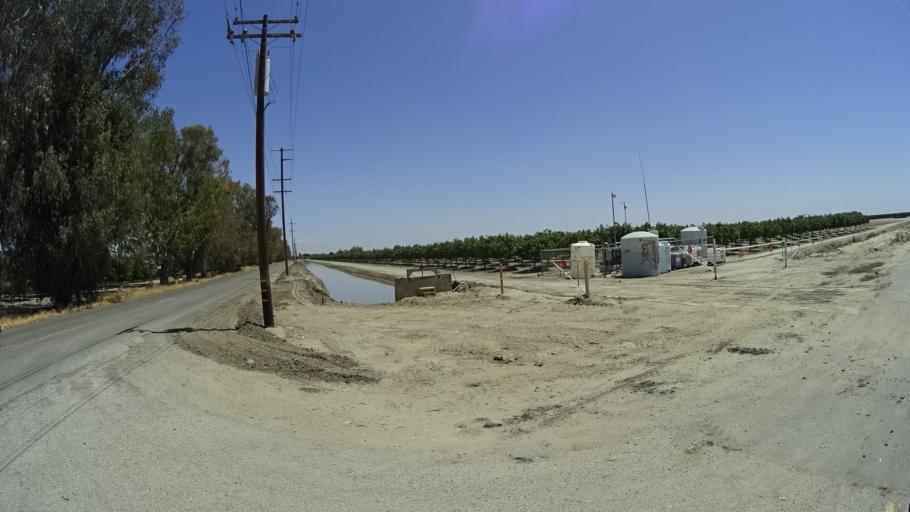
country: US
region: California
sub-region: Kings County
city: Corcoran
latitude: 36.1090
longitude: -119.5989
